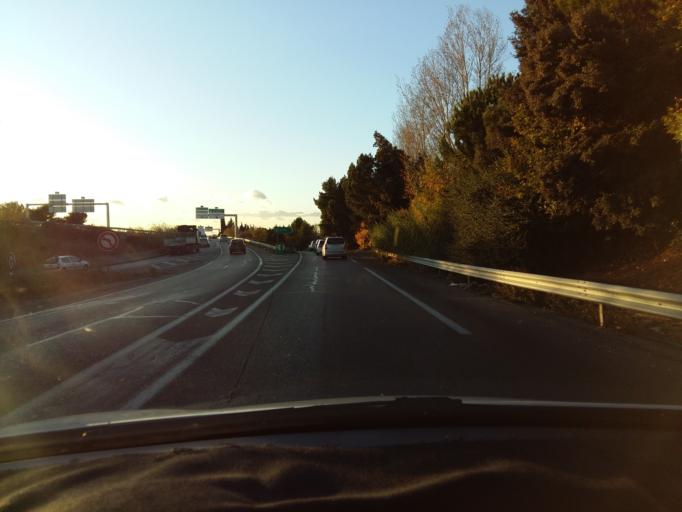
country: FR
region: Provence-Alpes-Cote d'Azur
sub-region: Departement des Bouches-du-Rhone
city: Saint-Victoret
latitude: 43.4277
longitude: 5.2652
